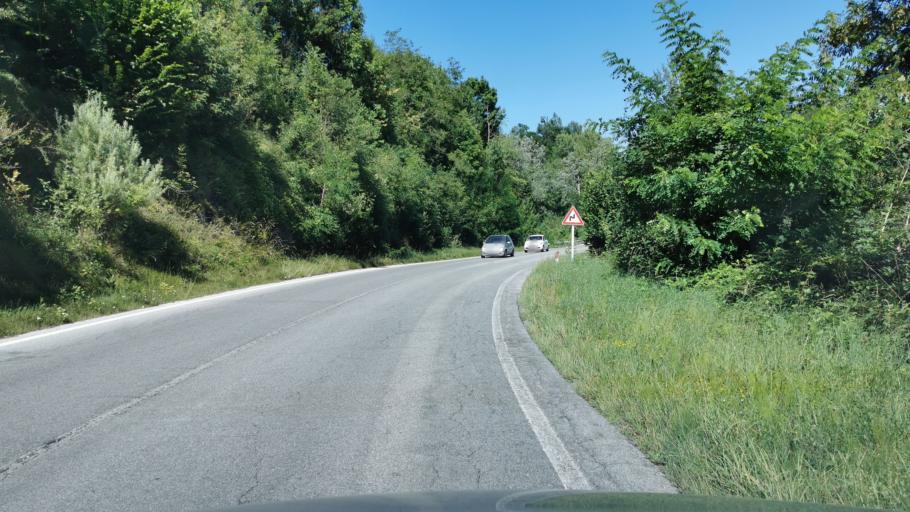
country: IT
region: Piedmont
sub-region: Provincia di Cuneo
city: Roccavione
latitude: 44.3140
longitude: 7.4597
